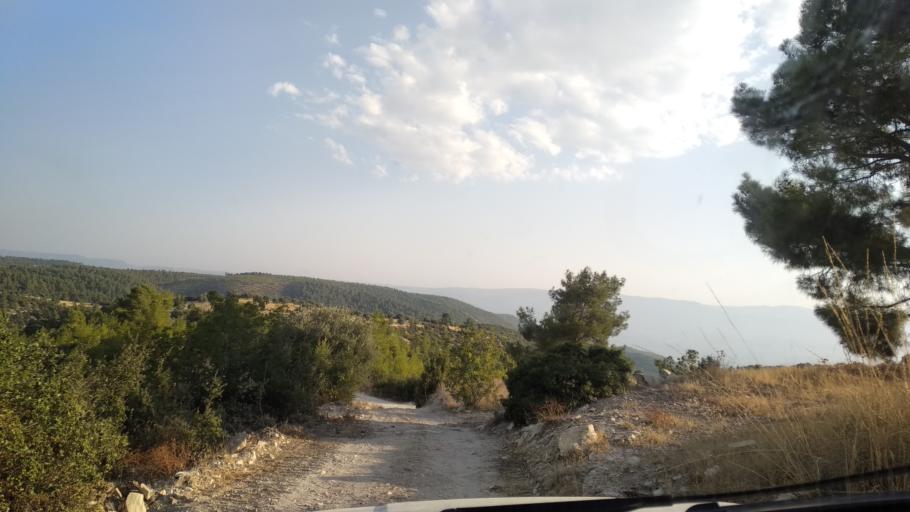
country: TR
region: Mersin
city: Sarikavak
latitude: 36.5603
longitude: 33.6278
